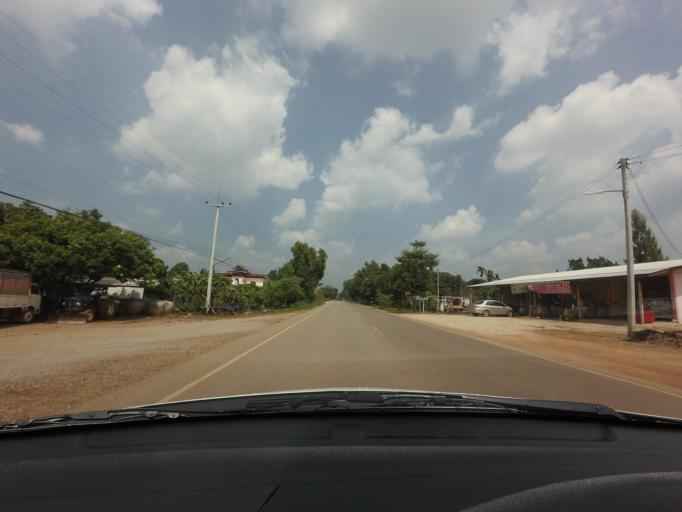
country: TH
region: Nakhon Ratchasima
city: Pak Chong
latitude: 14.5641
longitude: 101.5714
